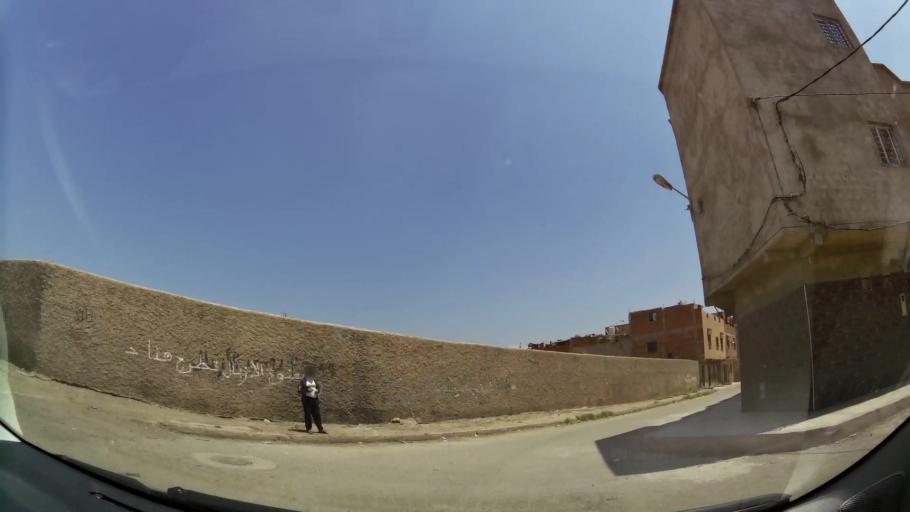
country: MA
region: Oriental
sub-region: Oujda-Angad
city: Oujda
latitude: 34.6834
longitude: -1.8918
